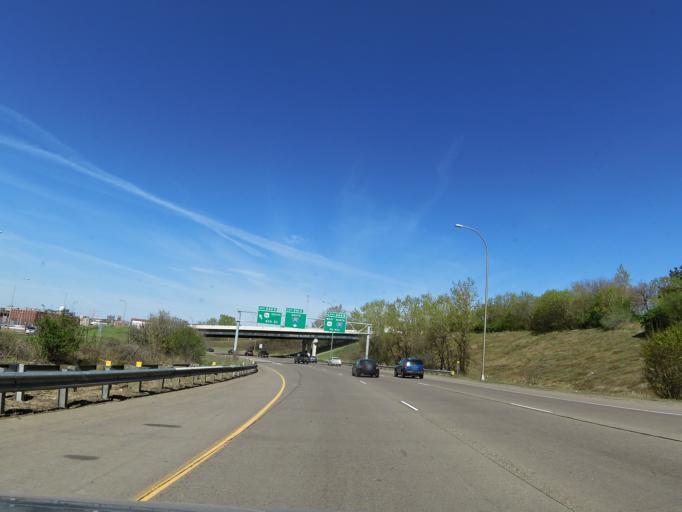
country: US
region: Minnesota
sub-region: Ramsey County
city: Saint Paul
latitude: 44.9550
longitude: -93.0734
